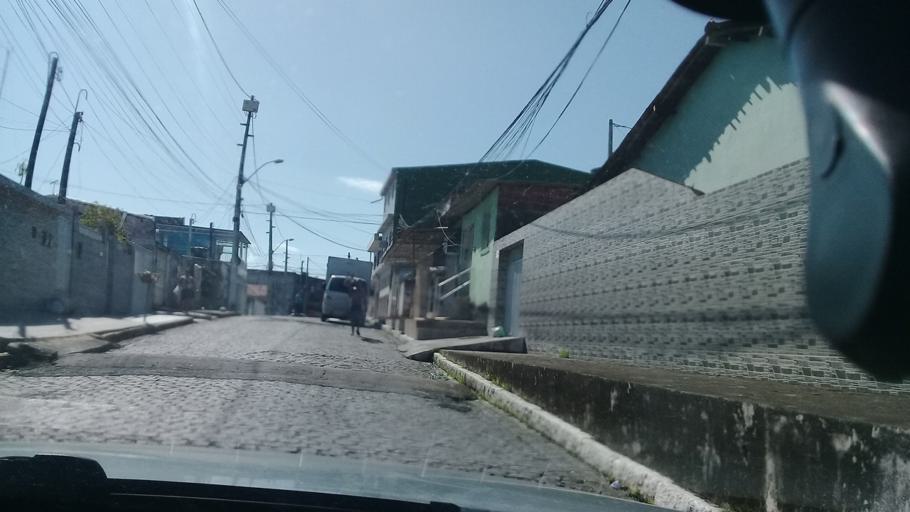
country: BR
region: Pernambuco
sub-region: Jaboatao Dos Guararapes
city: Jaboatao dos Guararapes
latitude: -8.1129
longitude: -34.9511
